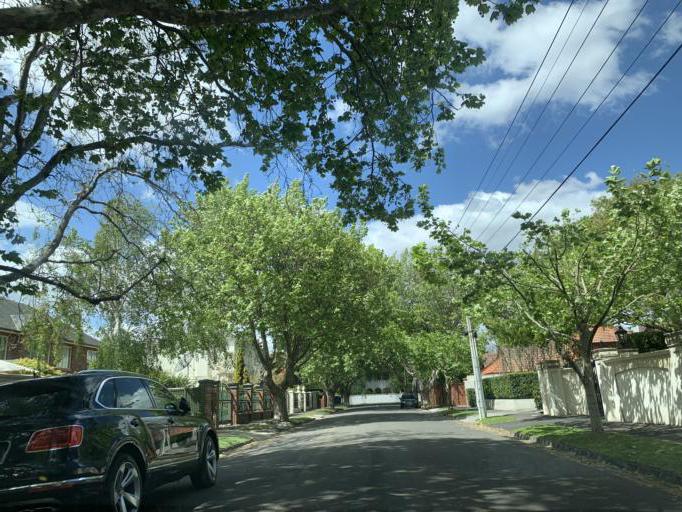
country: AU
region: Victoria
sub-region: Bayside
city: North Brighton
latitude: -37.9002
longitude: 144.9878
